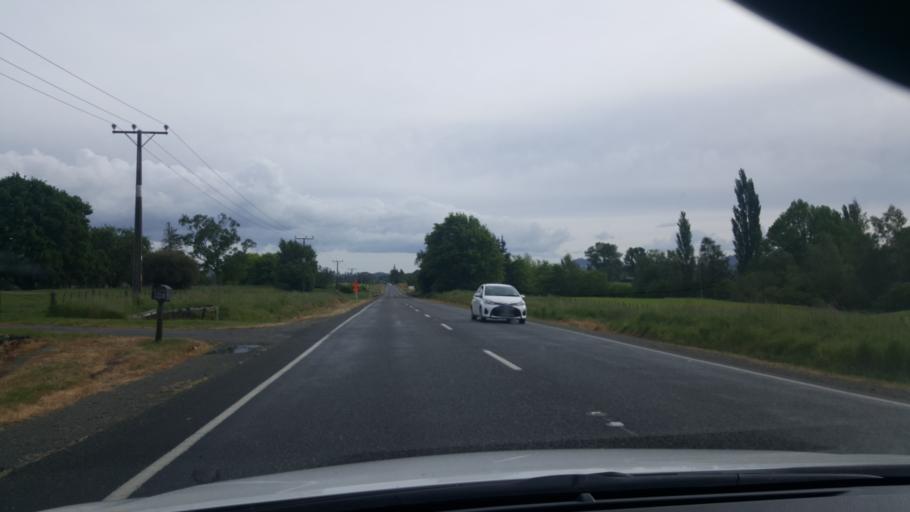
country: NZ
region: Bay of Plenty
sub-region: Rotorua District
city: Rotorua
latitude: -38.3986
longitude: 176.3334
